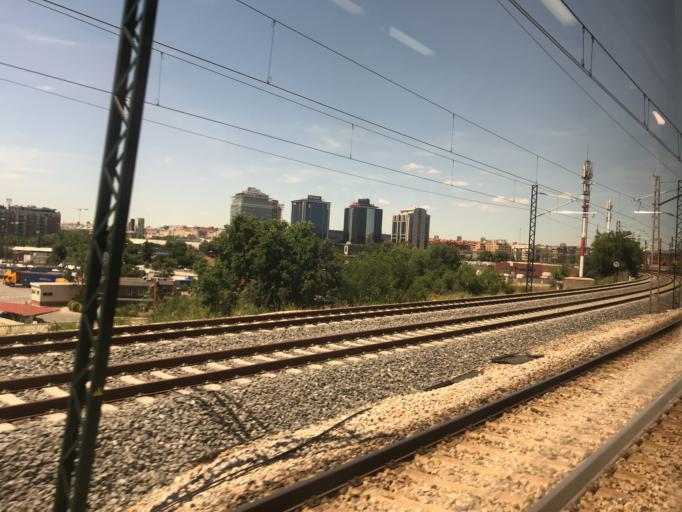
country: ES
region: Madrid
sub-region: Provincia de Madrid
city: Puente de Vallecas
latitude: 40.3889
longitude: -3.6743
